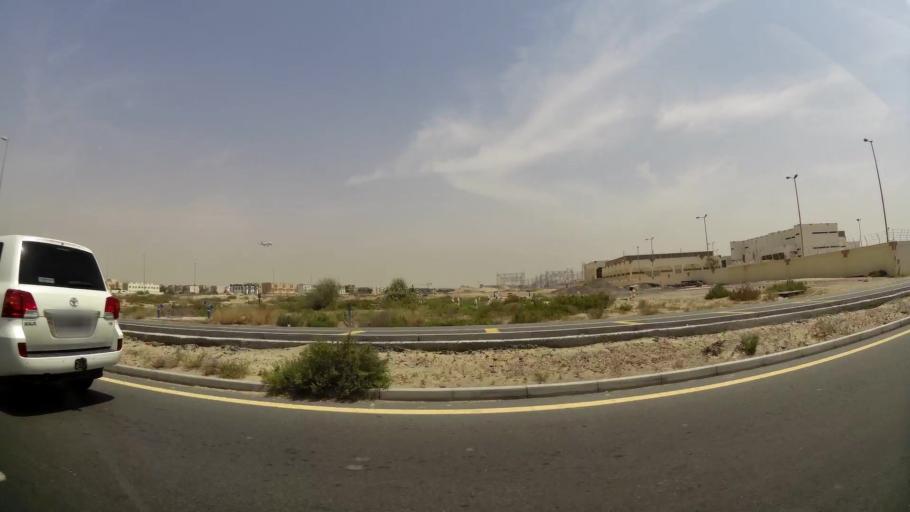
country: AE
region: Ash Shariqah
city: Sharjah
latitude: 25.2345
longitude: 55.4091
